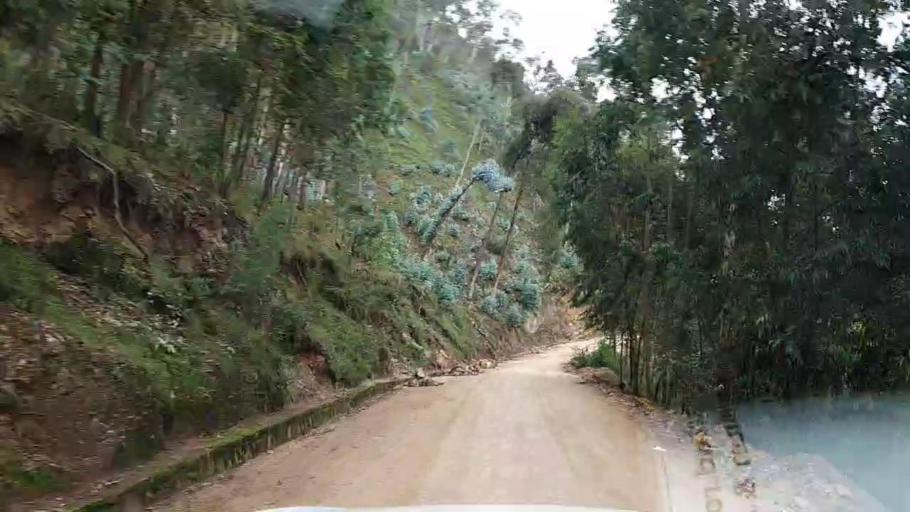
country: RW
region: Southern Province
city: Nzega
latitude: -2.3804
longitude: 29.4491
